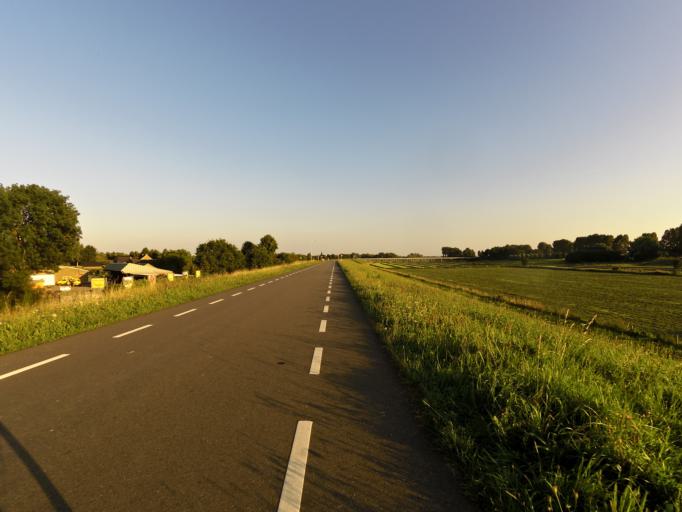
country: NL
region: Gelderland
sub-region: Gemeente Duiven
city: Duiven
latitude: 51.8962
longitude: 6.0279
